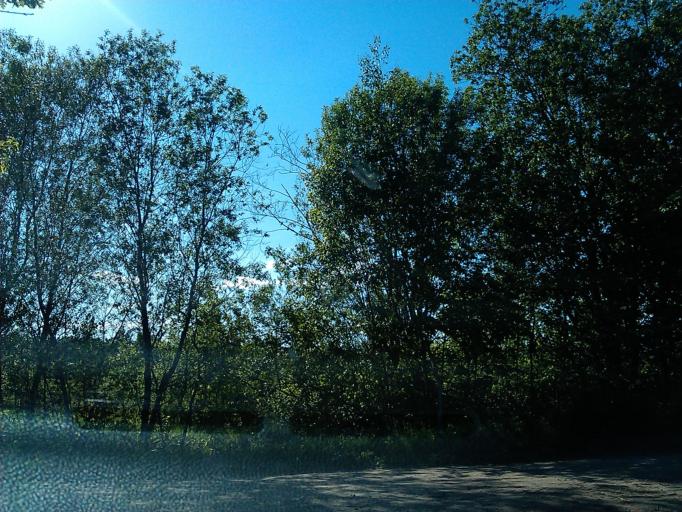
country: LV
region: Adazi
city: Adazi
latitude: 57.0944
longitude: 24.3248
